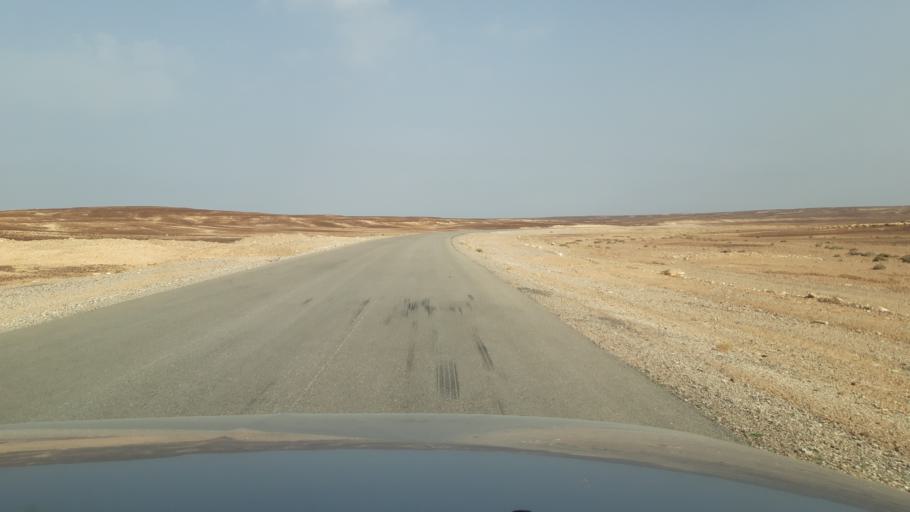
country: JO
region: Amman
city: Al Azraq ash Shamali
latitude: 31.2769
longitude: 36.5853
